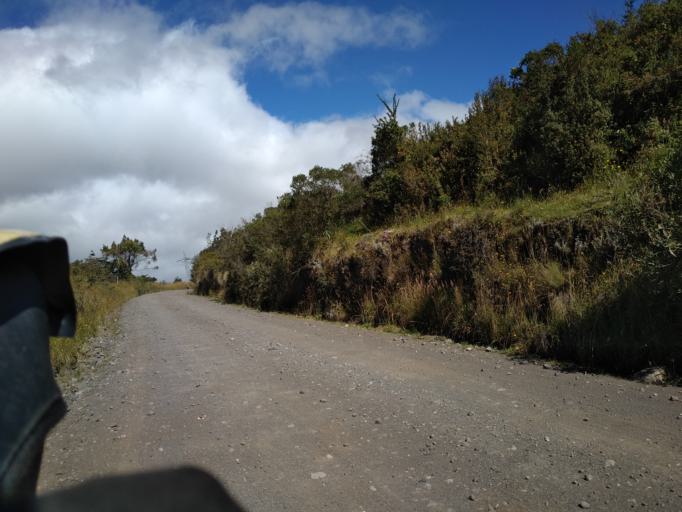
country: EC
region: Pichincha
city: Machachi
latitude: -0.5349
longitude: -78.4786
